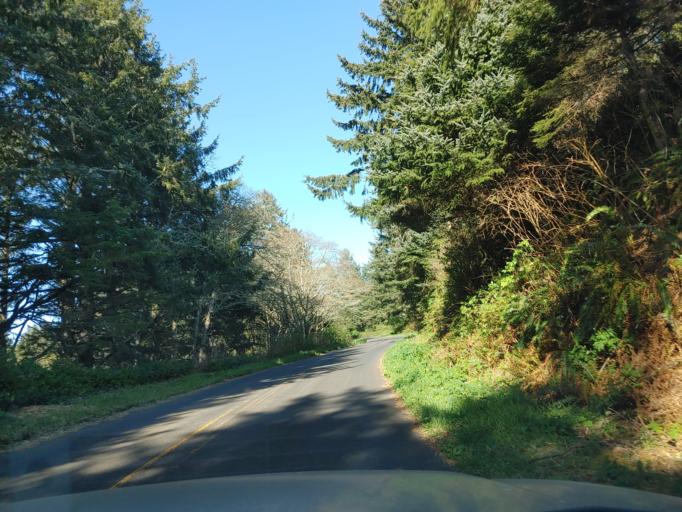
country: US
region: Oregon
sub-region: Lincoln County
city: Depoe Bay
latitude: 44.7618
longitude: -124.0647
